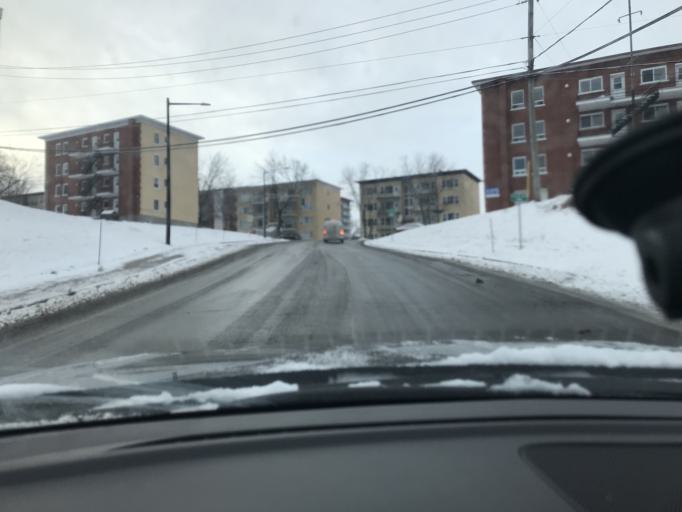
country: CA
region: Quebec
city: Quebec
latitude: 46.7923
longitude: -71.2735
